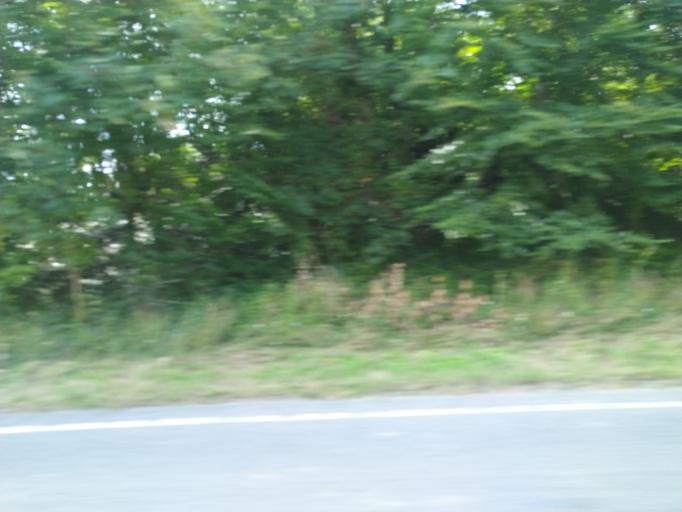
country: GB
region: England
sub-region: Dorset
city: Blandford Forum
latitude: 50.8631
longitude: -2.1475
